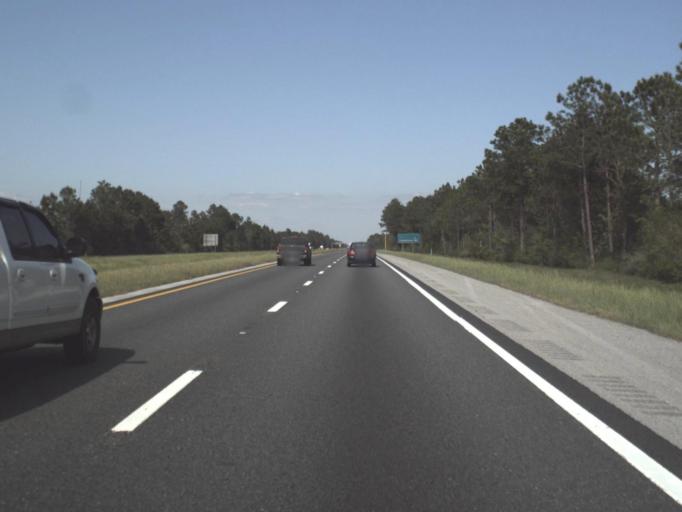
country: US
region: Florida
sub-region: Santa Rosa County
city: Bagdad
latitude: 30.5369
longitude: -87.0740
